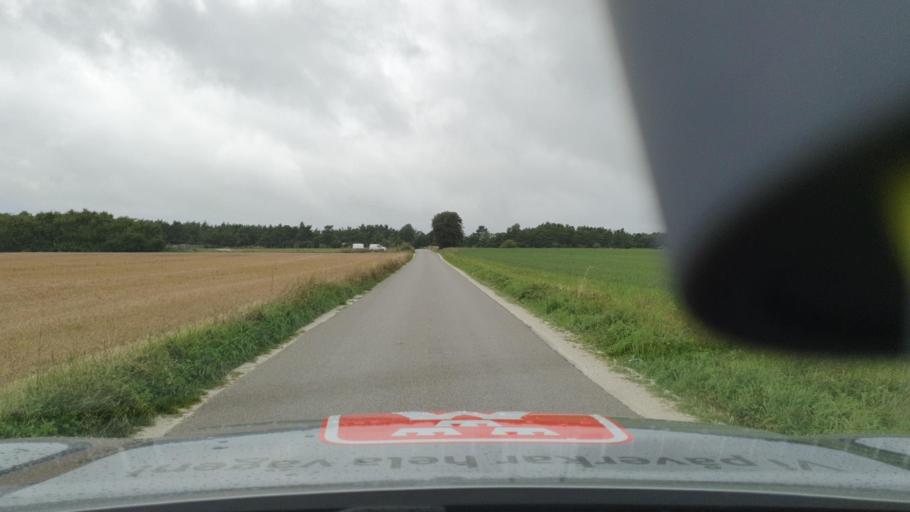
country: SE
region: Gotland
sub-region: Gotland
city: Hemse
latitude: 56.9441
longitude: 18.2586
